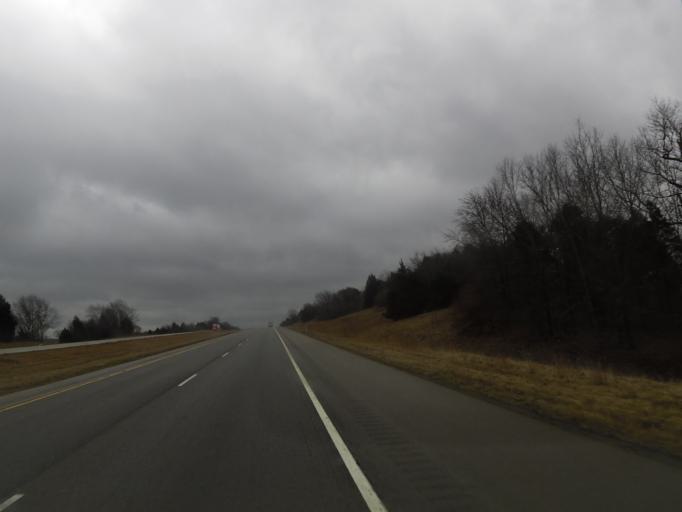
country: US
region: Illinois
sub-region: Johnson County
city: Goreville
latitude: 37.5731
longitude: -88.9585
